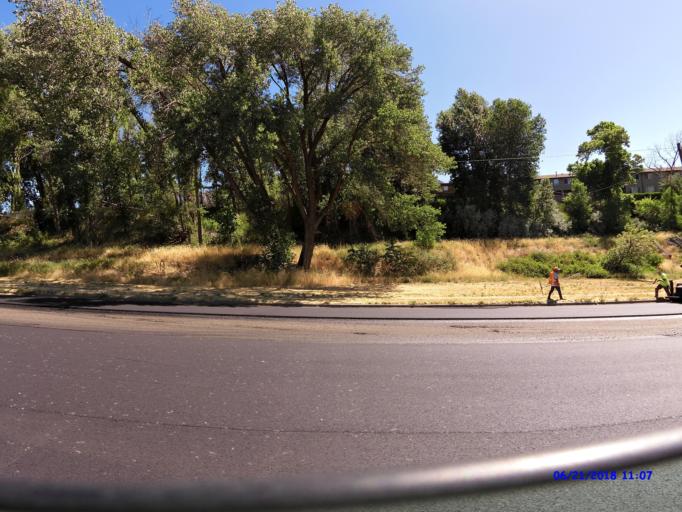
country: US
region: Utah
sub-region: Weber County
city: Ogden
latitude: 41.2467
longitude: -111.9544
